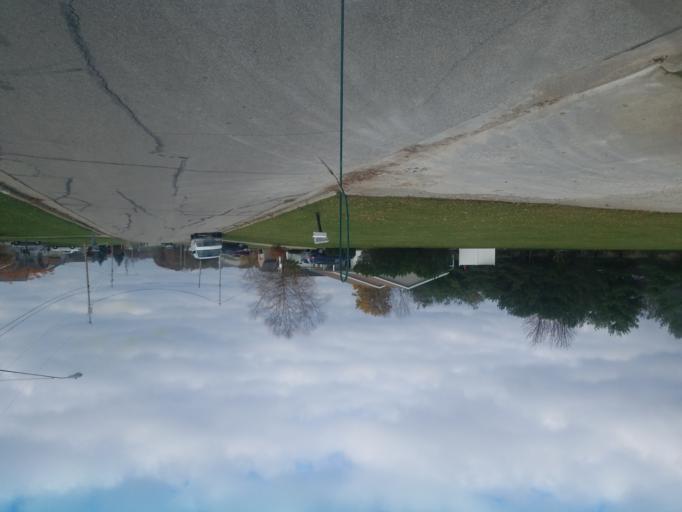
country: US
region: Ohio
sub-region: Richland County
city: Ontario
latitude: 40.7886
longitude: -82.5768
